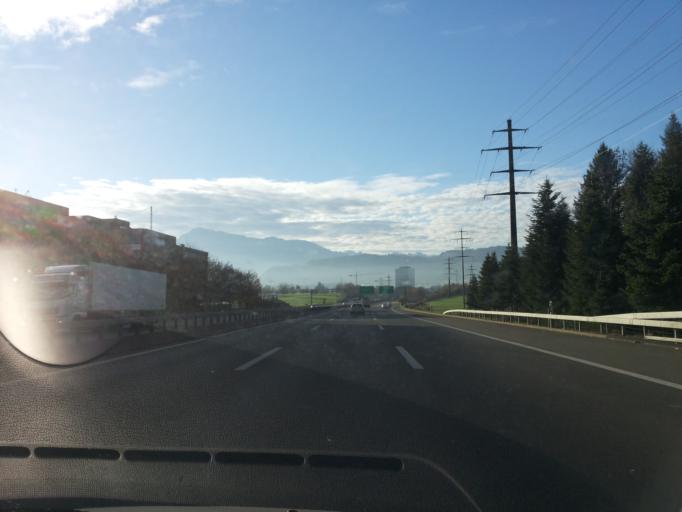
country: CH
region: Zug
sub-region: Zug
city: Hunenberg
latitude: 47.1633
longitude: 8.4327
